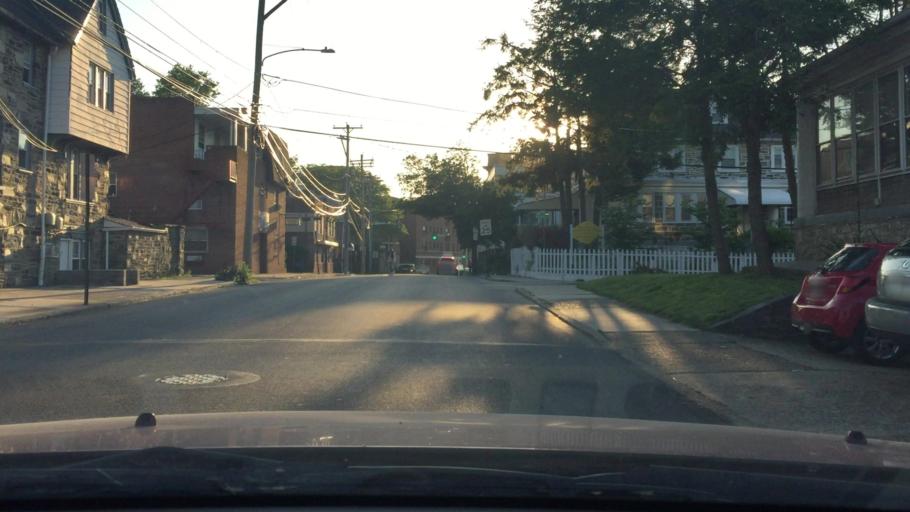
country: US
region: Pennsylvania
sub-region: Delaware County
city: Millbourne
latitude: 39.9594
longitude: -75.2614
